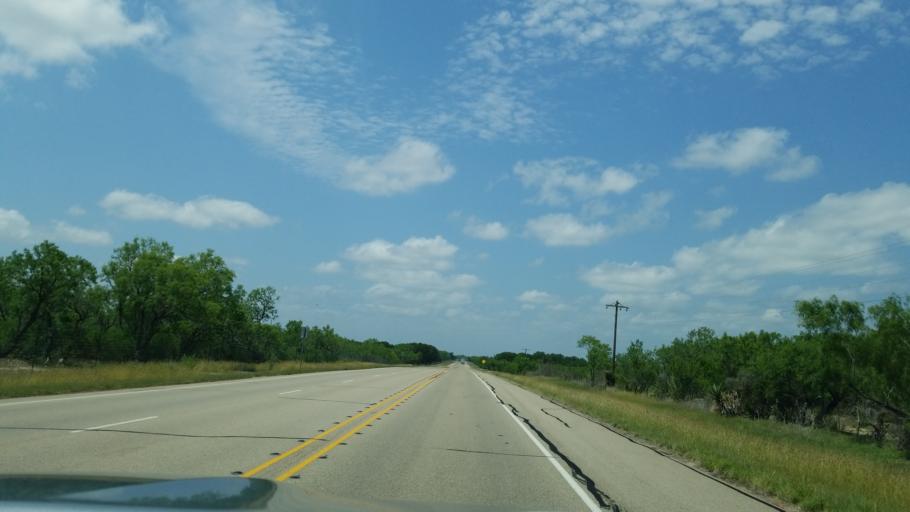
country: US
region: Texas
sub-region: Frio County
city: Pearsall
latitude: 29.0028
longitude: -99.2159
